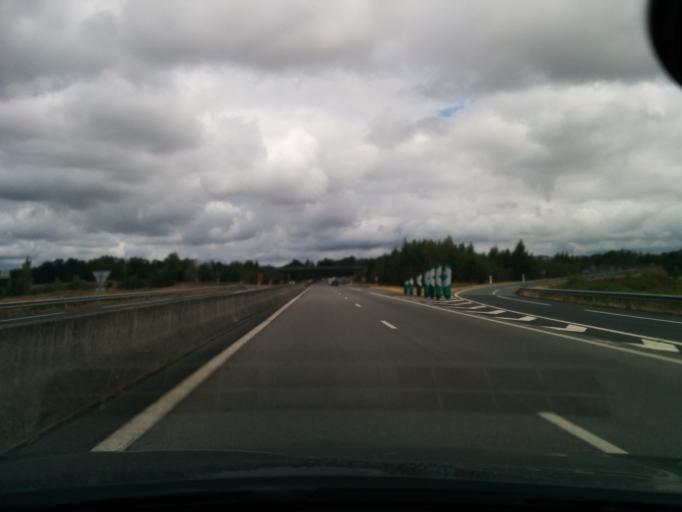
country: FR
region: Limousin
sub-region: Departement de la Correze
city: Ussac
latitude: 45.1845
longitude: 1.4919
